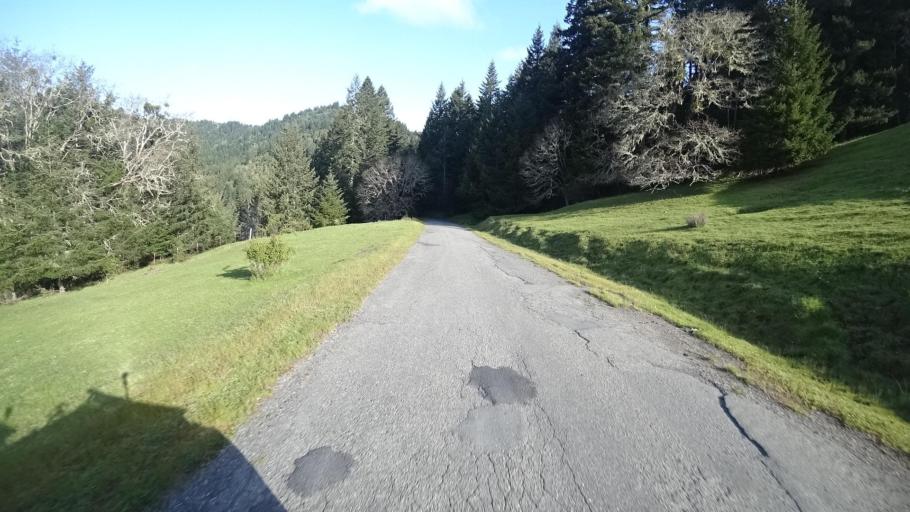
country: US
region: California
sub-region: Humboldt County
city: Bayside
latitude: 40.6916
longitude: -123.9408
